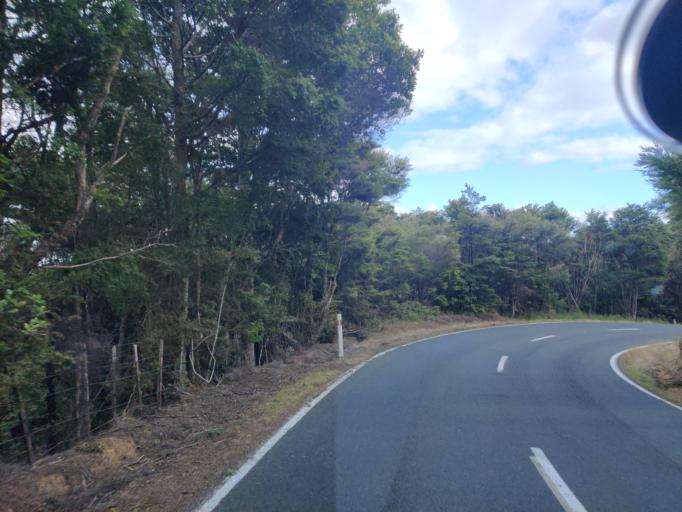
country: NZ
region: Northland
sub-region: Whangarei
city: Ngunguru
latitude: -35.5793
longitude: 174.4096
